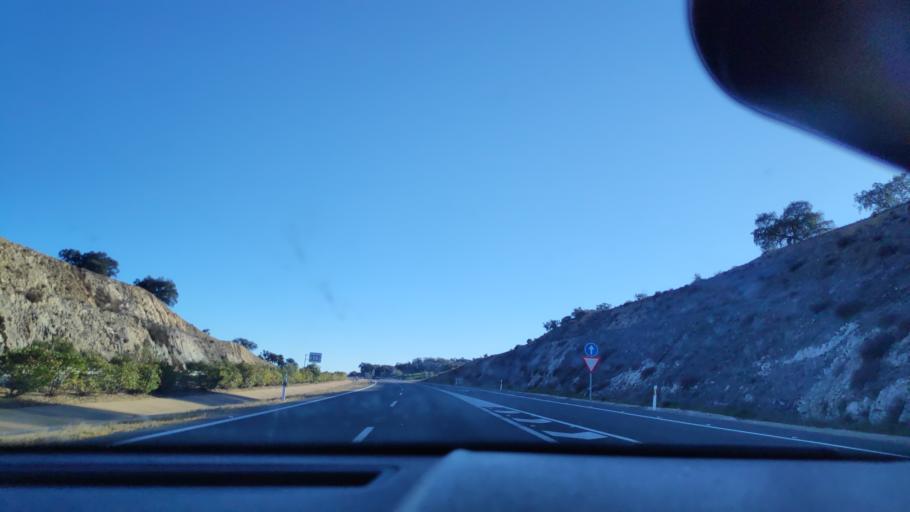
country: ES
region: Extremadura
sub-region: Provincia de Badajoz
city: Monesterio
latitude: 38.1320
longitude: -6.2743
